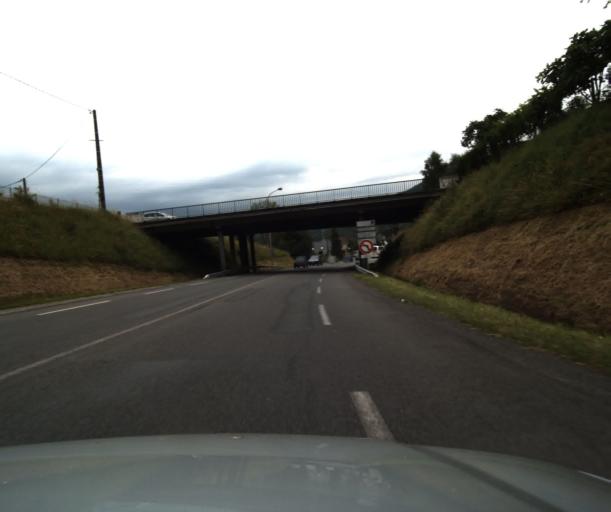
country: FR
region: Midi-Pyrenees
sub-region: Departement des Hautes-Pyrenees
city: Lourdes
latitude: 43.1028
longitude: -0.0300
